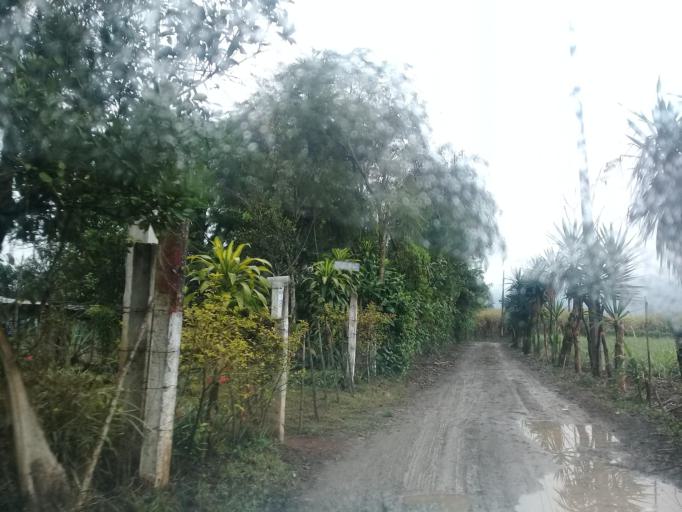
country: MX
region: Veracruz
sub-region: Amatlan de los Reyes
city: Centro de Readaptacion Social
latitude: 18.8198
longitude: -96.9447
